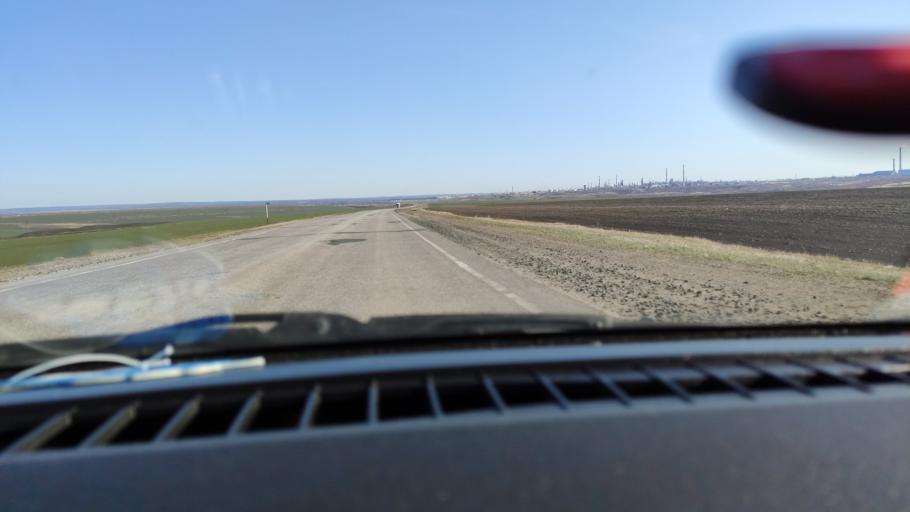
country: RU
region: Samara
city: Varlamovo
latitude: 53.0385
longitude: 48.3377
